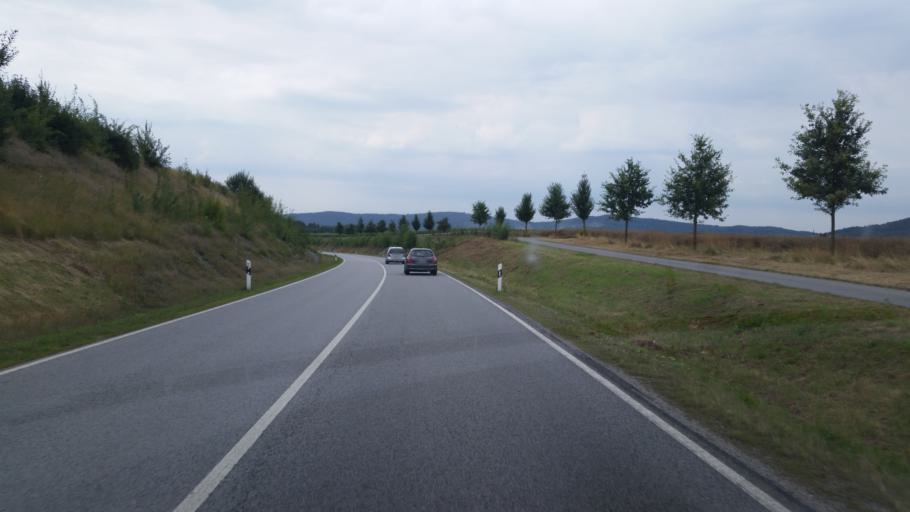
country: DE
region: Saxony
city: Elstra
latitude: 51.2298
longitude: 14.1481
